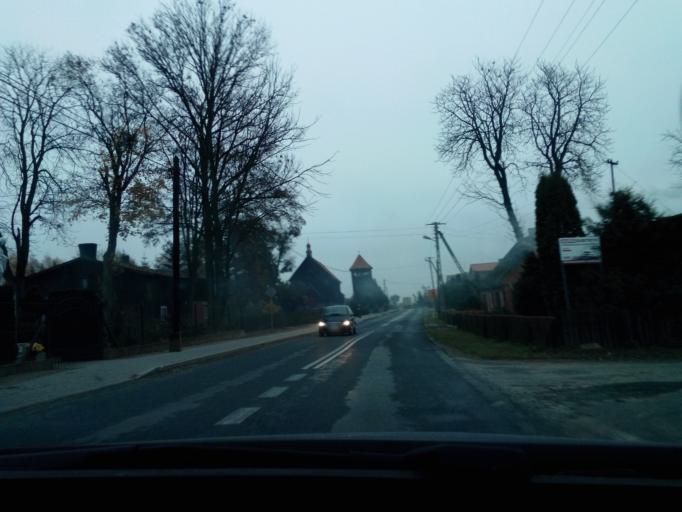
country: PL
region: Kujawsko-Pomorskie
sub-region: Powiat brodnicki
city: Bartniczka
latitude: 53.2494
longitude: 19.5700
